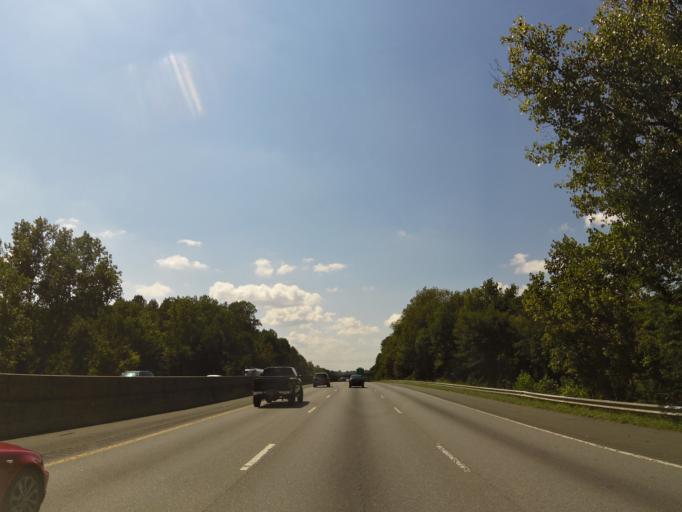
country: US
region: North Carolina
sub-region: Gaston County
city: Cramerton
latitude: 35.2642
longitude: -81.0646
